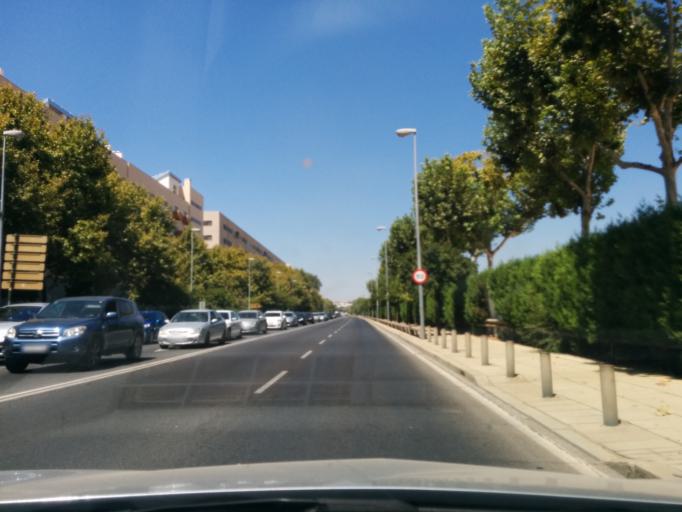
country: ES
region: Andalusia
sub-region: Provincia de Sevilla
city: Sevilla
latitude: 37.3679
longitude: -5.9984
